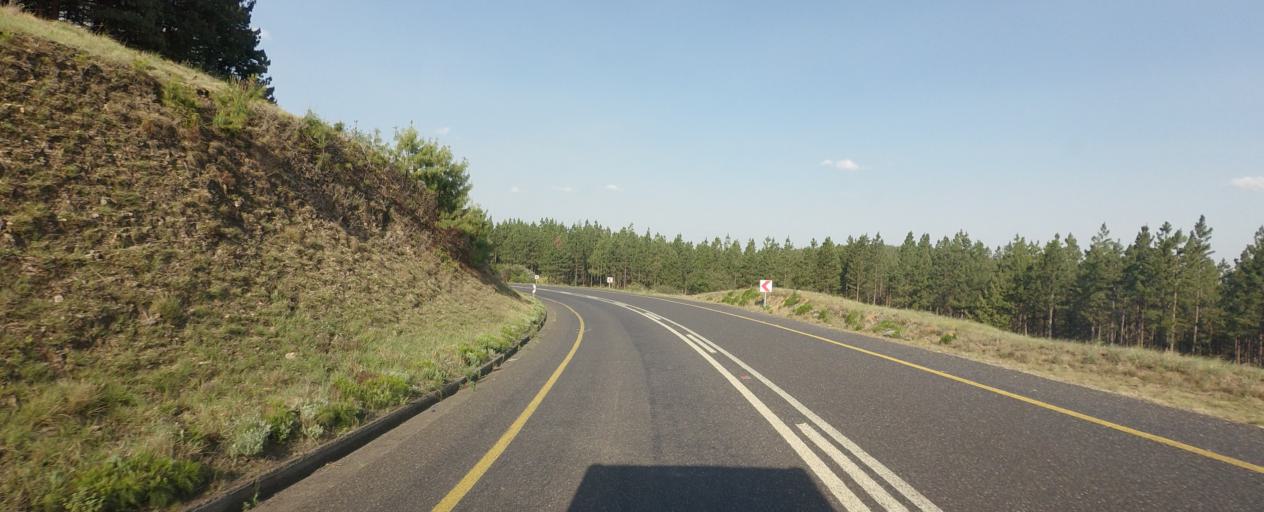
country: ZA
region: Mpumalanga
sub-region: Ehlanzeni District
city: Lydenburg
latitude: -25.1638
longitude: 30.6334
